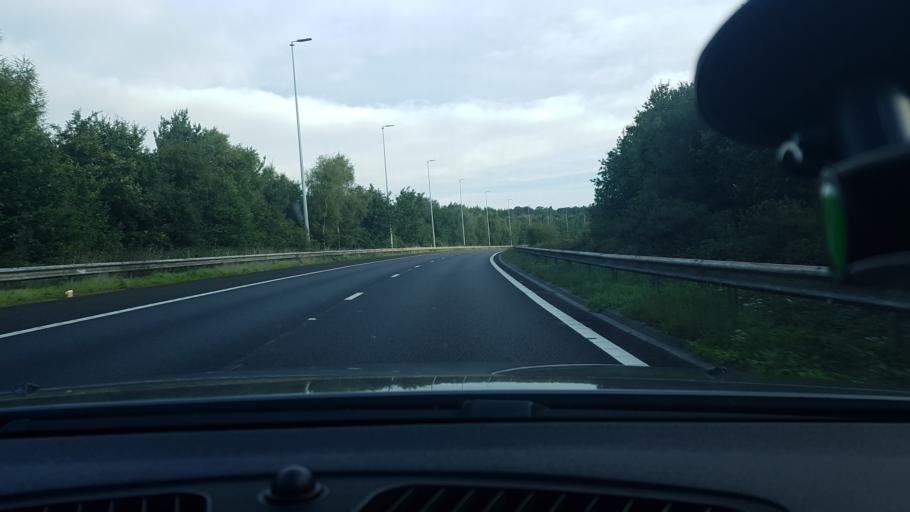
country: GB
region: England
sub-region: Southampton
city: Southampton
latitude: 50.9518
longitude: -1.4002
